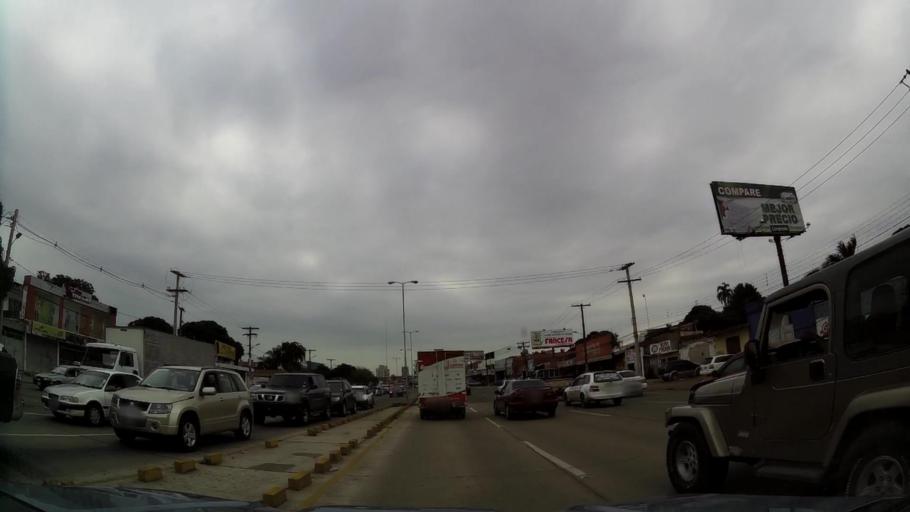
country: BO
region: Santa Cruz
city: Santa Cruz de la Sierra
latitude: -17.7762
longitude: -63.1663
